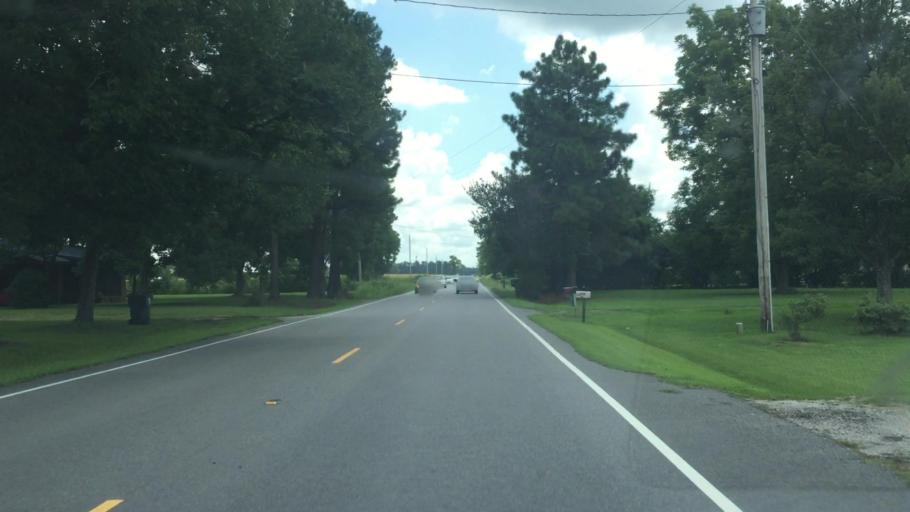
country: US
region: North Carolina
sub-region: Columbus County
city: Chadbourn
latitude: 34.2890
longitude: -78.8236
